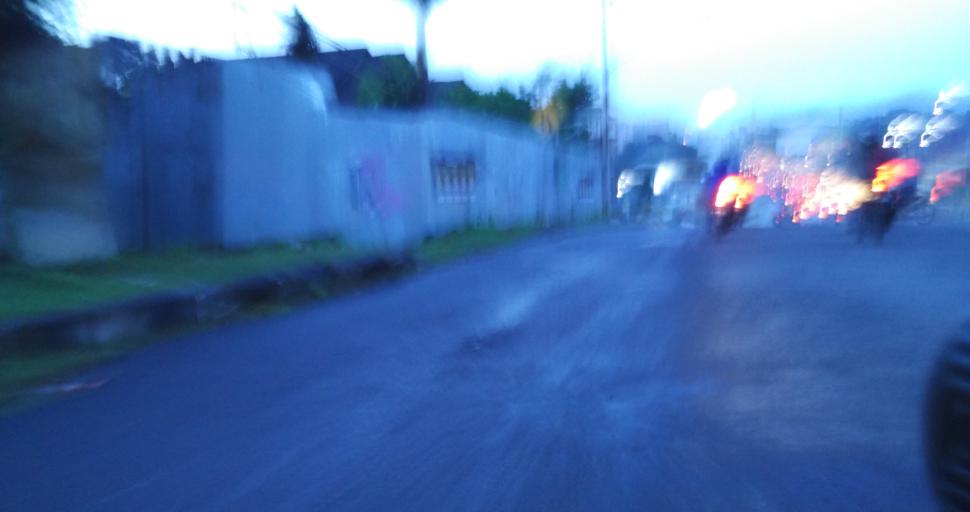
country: ID
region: Central Java
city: Semarang
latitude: -7.0348
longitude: 110.4174
